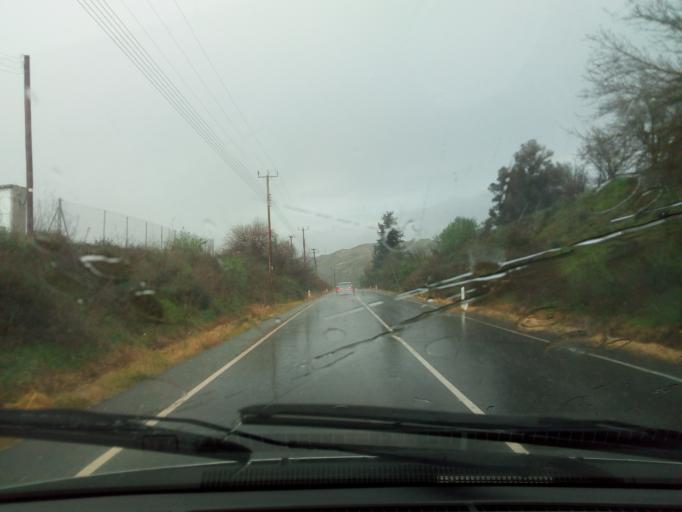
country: CY
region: Pafos
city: Polis
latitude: 34.9480
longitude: 32.4678
